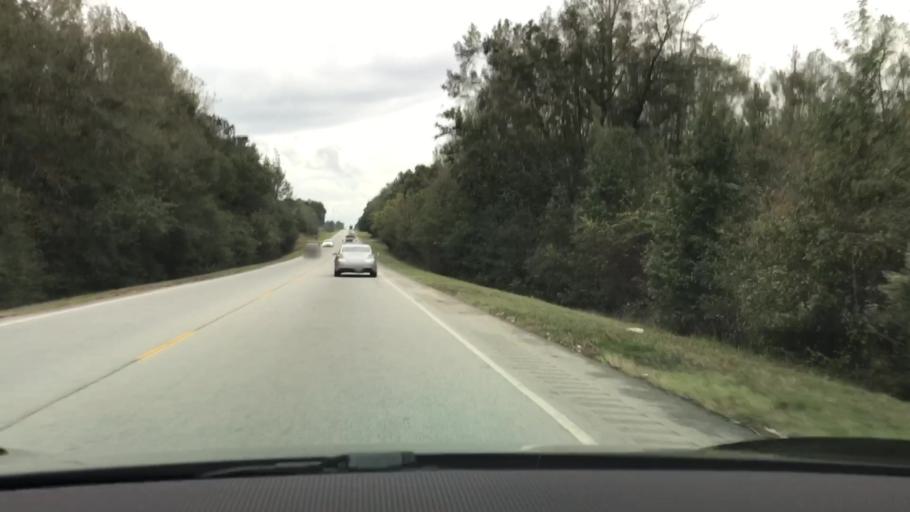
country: US
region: Georgia
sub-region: Jefferson County
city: Louisville
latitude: 32.9430
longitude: -82.3954
